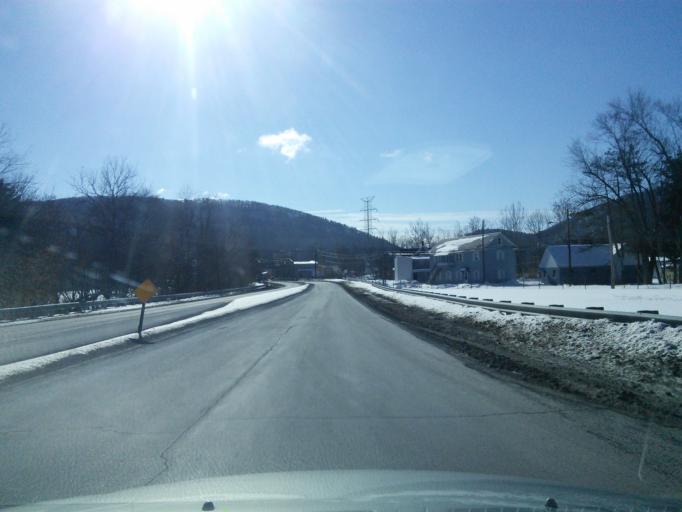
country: US
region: Pennsylvania
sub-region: Centre County
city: Milesburg
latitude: 40.9447
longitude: -77.7880
